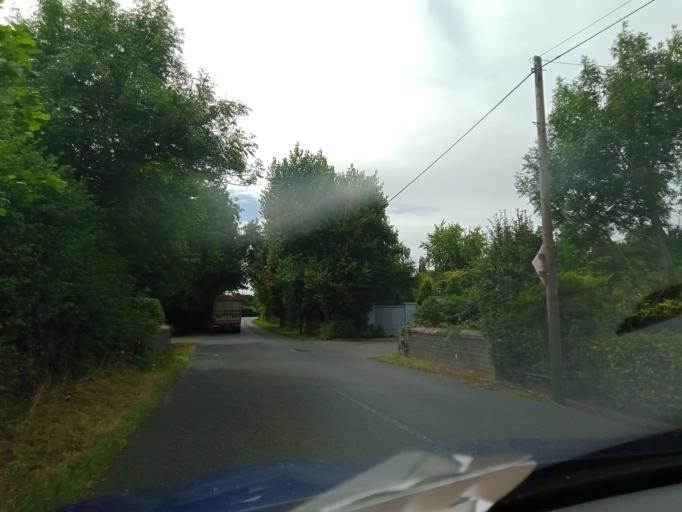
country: IE
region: Leinster
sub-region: Laois
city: Portlaoise
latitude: 53.0167
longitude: -7.2951
